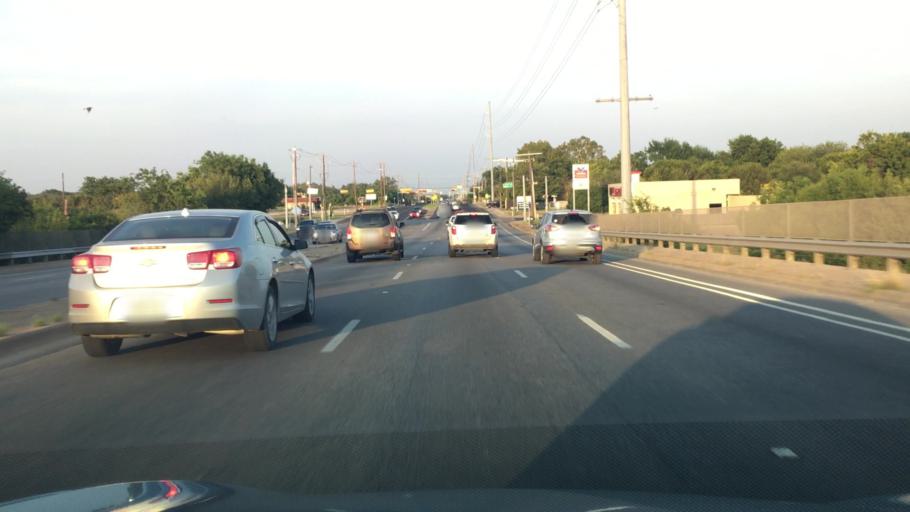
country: US
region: Texas
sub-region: Travis County
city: Manchaca
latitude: 30.1737
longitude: -97.8184
